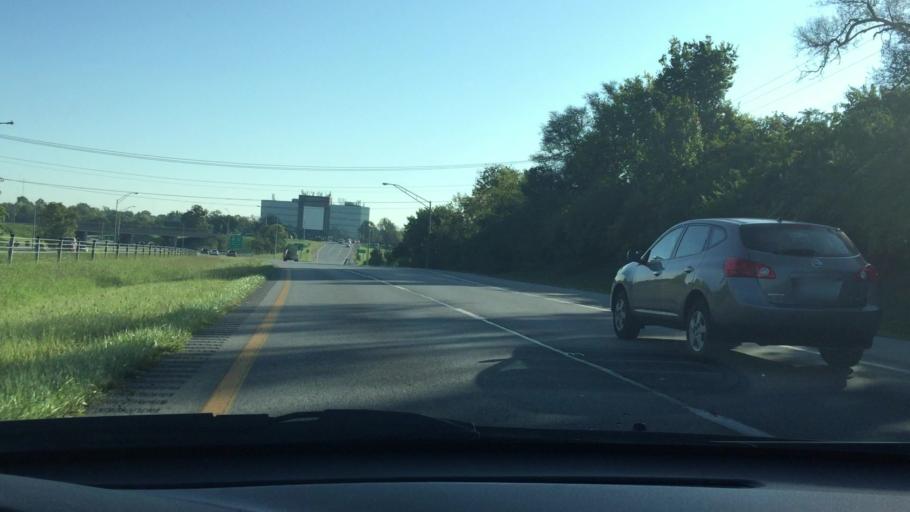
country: US
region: Kentucky
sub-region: Fayette County
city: Lexington
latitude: 37.9935
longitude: -84.4696
